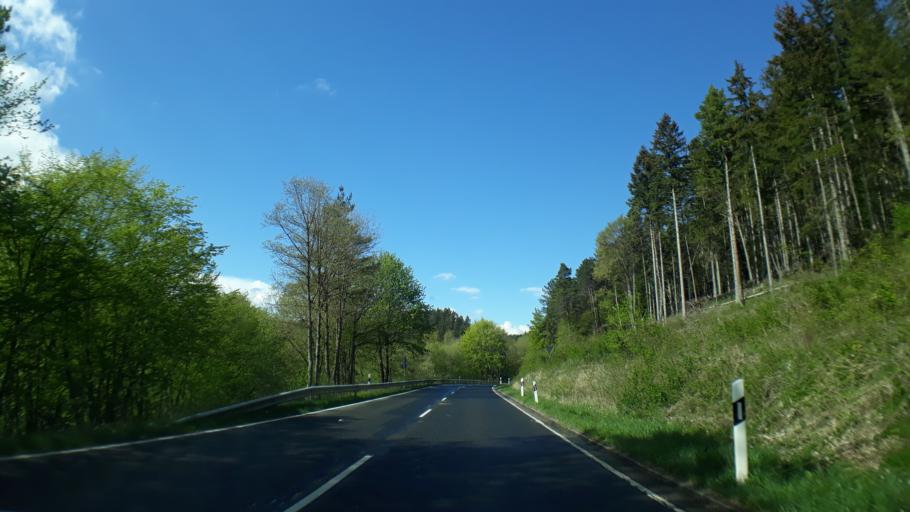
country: DE
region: North Rhine-Westphalia
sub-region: Regierungsbezirk Koln
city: Kall
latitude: 50.5162
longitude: 6.5651
